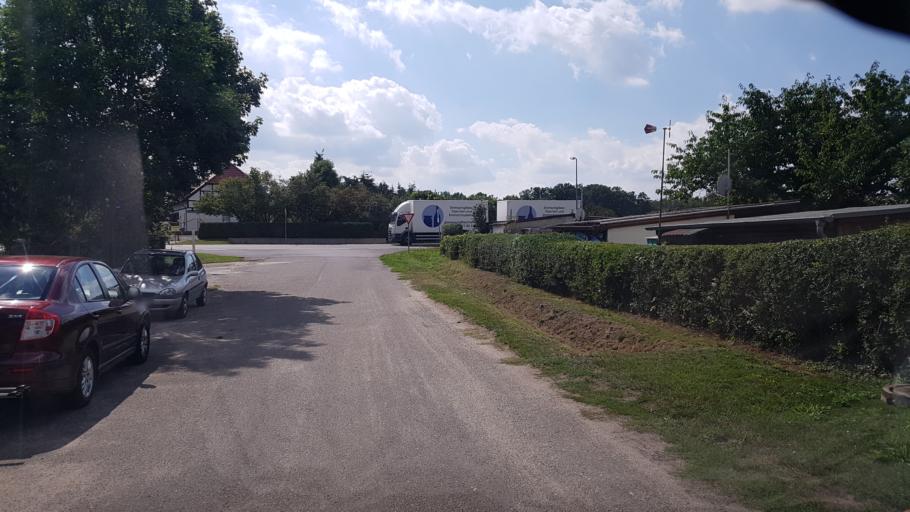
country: DE
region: Brandenburg
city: Lubbenau
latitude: 51.8652
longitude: 13.9272
